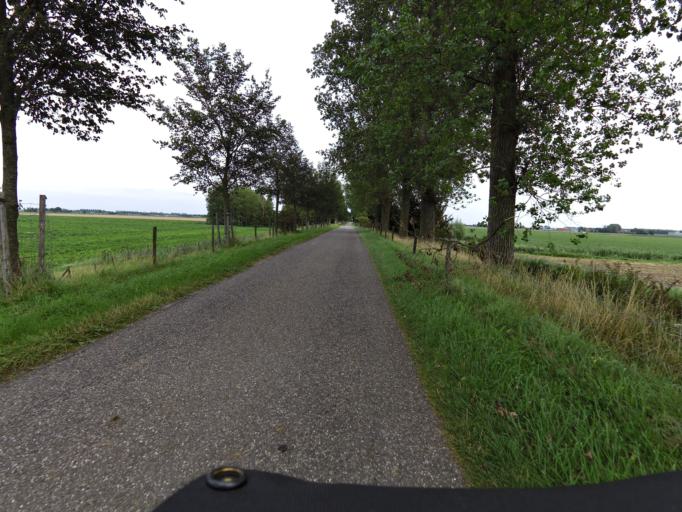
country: NL
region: South Holland
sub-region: Gemeente Goeree-Overflakkee
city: Middelharnis
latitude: 51.7105
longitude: 4.1989
